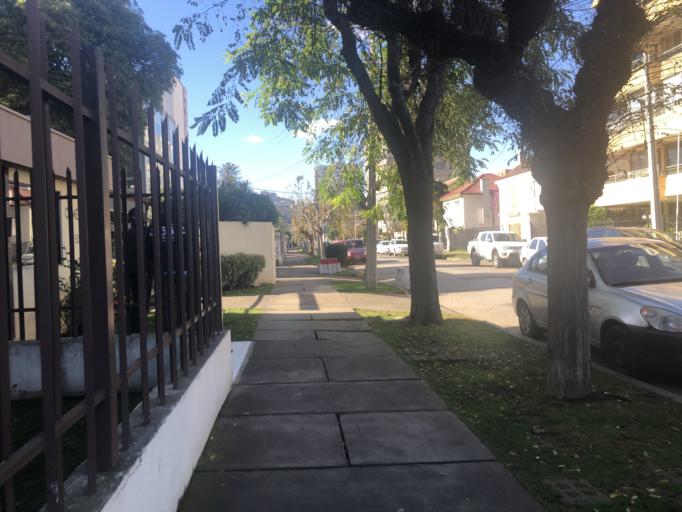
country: CL
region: Valparaiso
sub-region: Provincia de Valparaiso
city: Vina del Mar
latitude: -33.0207
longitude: -71.5496
